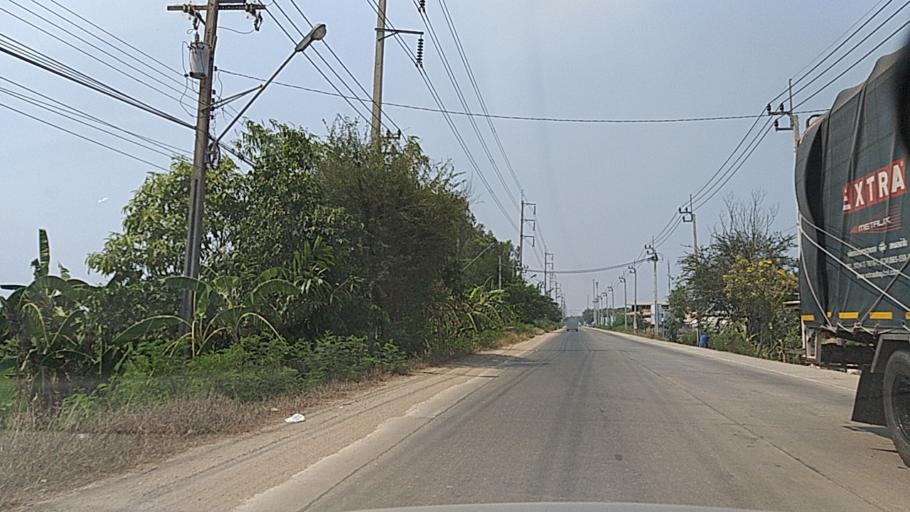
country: TH
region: Nonthaburi
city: Sai Noi
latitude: 13.9348
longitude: 100.3170
